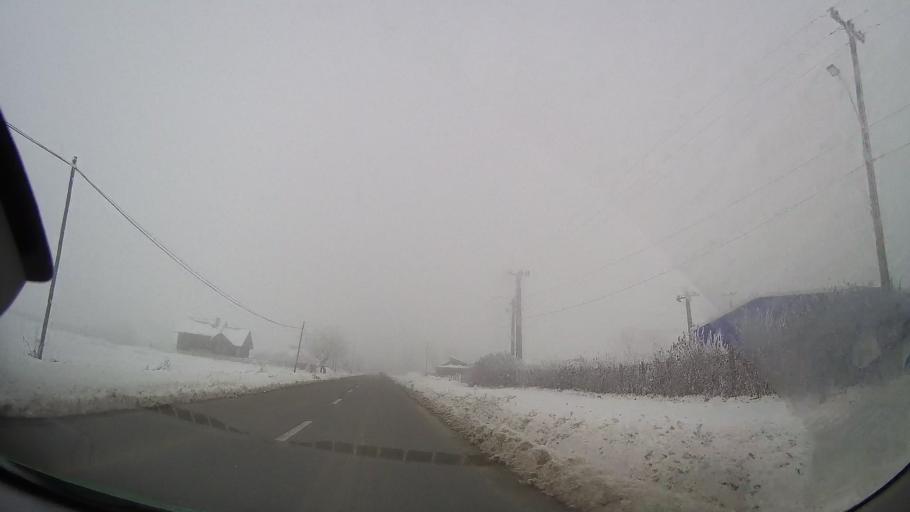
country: RO
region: Iasi
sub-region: Comuna Stolniceni-Prajescu
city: Stolniceni-Prajescu
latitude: 47.1981
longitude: 26.7391
